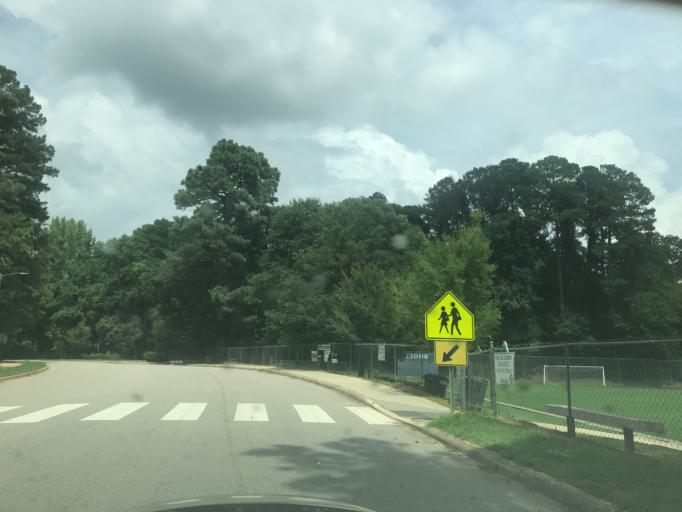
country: US
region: North Carolina
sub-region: Wake County
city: West Raleigh
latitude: 35.8179
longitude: -78.6343
